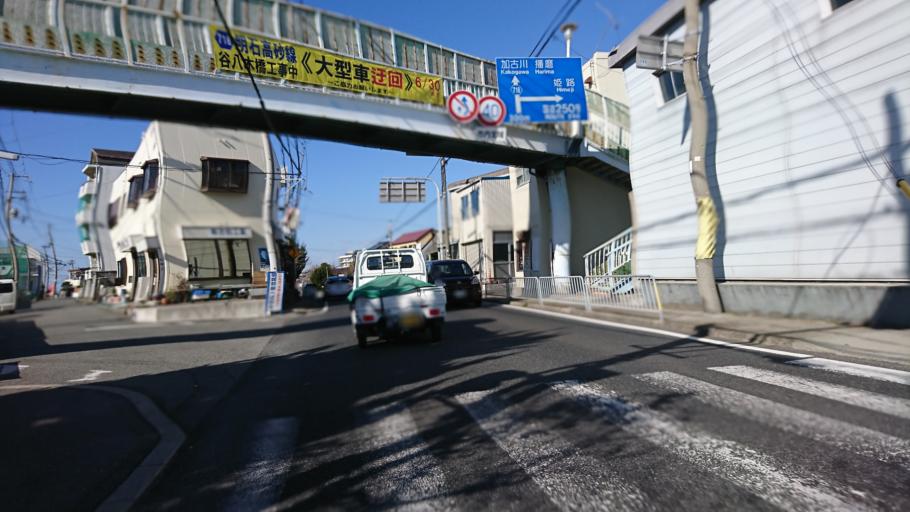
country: JP
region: Hyogo
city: Akashi
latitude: 34.6581
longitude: 134.9539
